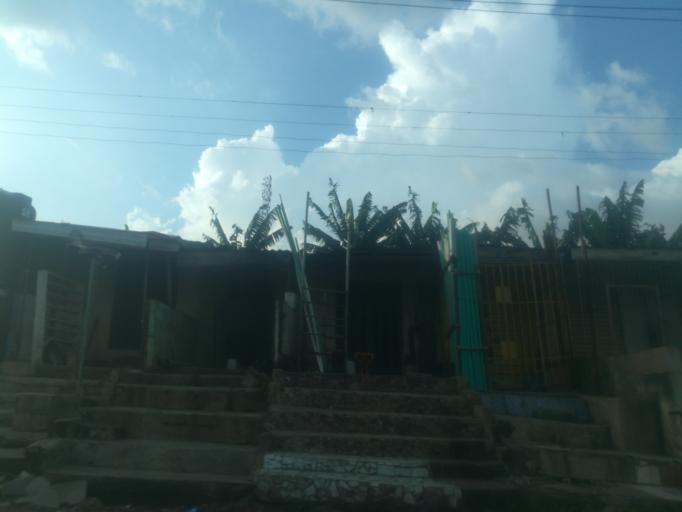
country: NG
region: Oyo
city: Ibadan
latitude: 7.3866
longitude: 3.8750
